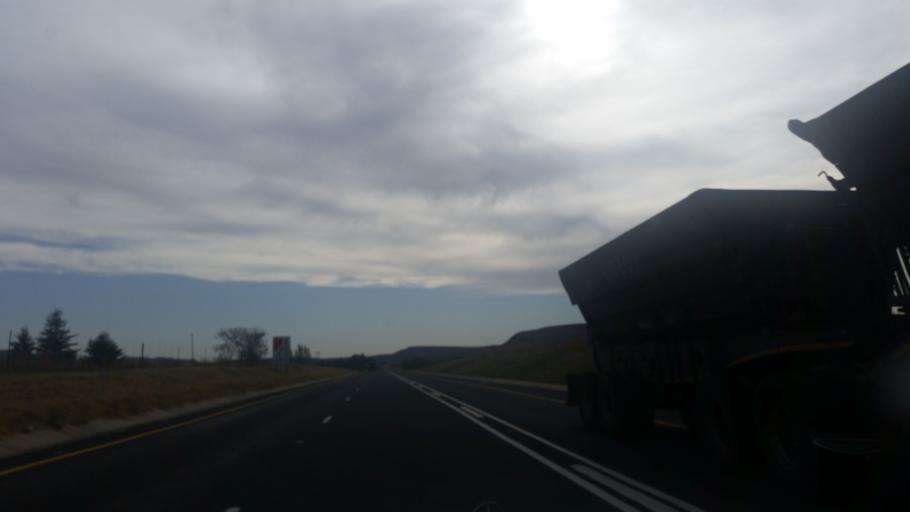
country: ZA
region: Orange Free State
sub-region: Thabo Mofutsanyana District Municipality
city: Phuthaditjhaba
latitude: -28.3127
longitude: 28.7427
